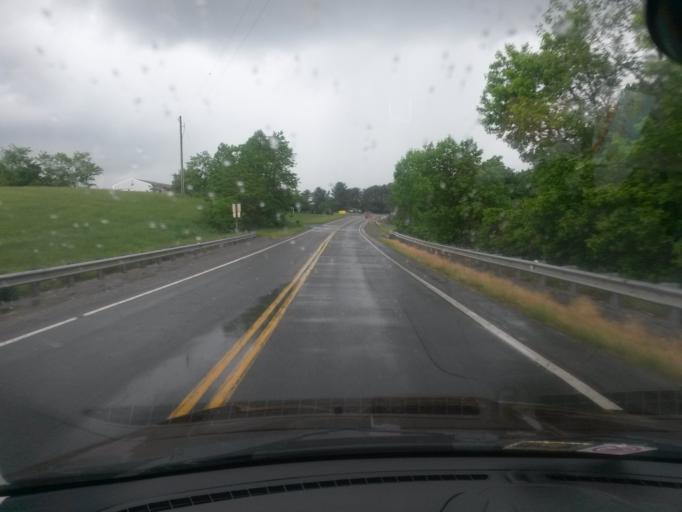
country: US
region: Virginia
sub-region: Floyd County
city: Floyd
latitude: 36.9702
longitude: -80.3908
